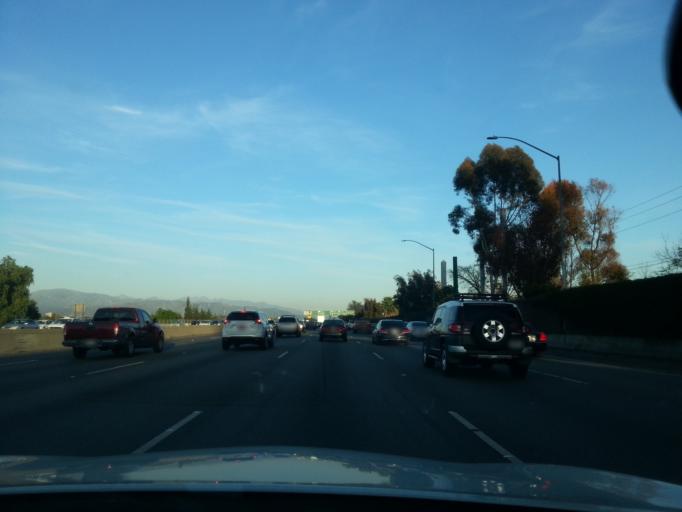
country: US
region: California
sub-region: Los Angeles County
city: Sherman Oaks
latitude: 34.1651
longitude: -118.4892
